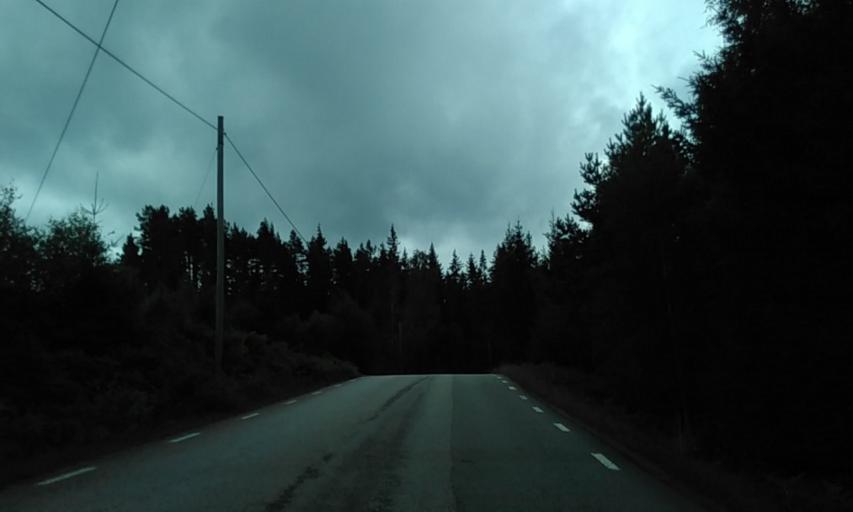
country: SE
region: Vaestra Goetaland
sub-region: Alingsas Kommun
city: Alingsas
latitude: 57.8373
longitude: 12.6533
